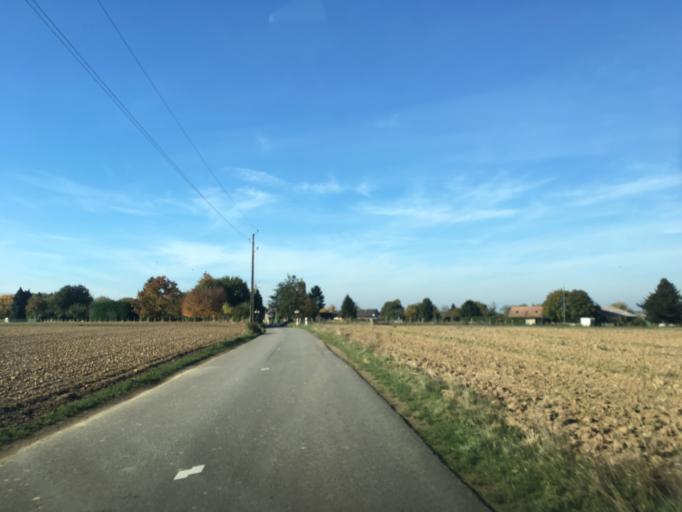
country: FR
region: Haute-Normandie
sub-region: Departement de l'Eure
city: Heudreville-sur-Eure
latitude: 49.1595
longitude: 1.2531
